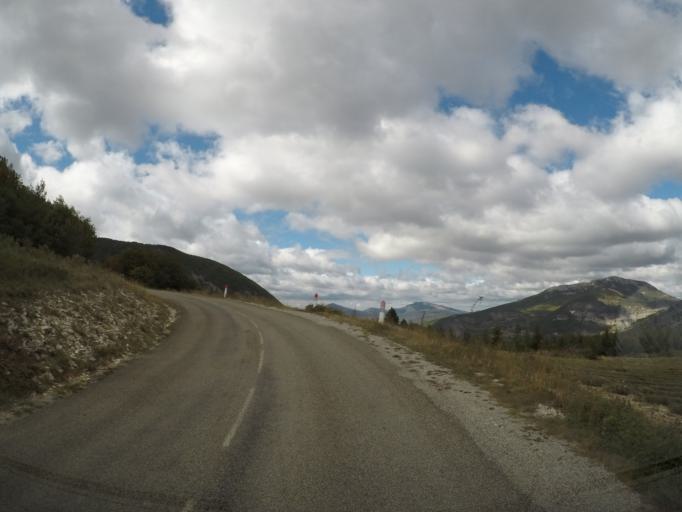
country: FR
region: Provence-Alpes-Cote d'Azur
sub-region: Departement du Vaucluse
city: Sault
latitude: 44.1743
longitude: 5.5055
